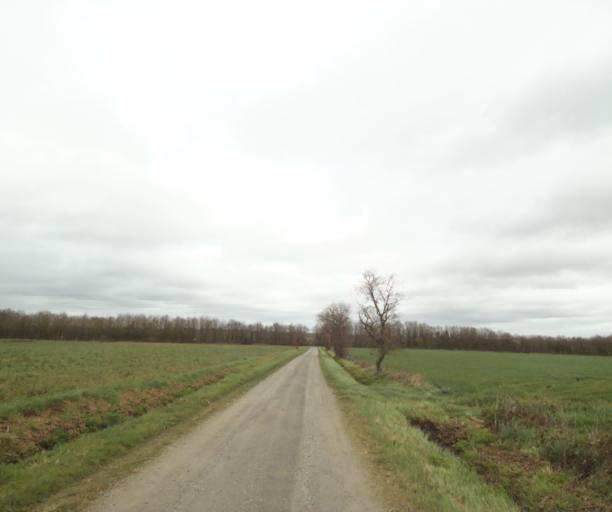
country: FR
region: Pays de la Loire
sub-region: Departement de la Loire-Atlantique
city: Bouvron
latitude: 47.4244
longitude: -1.8459
